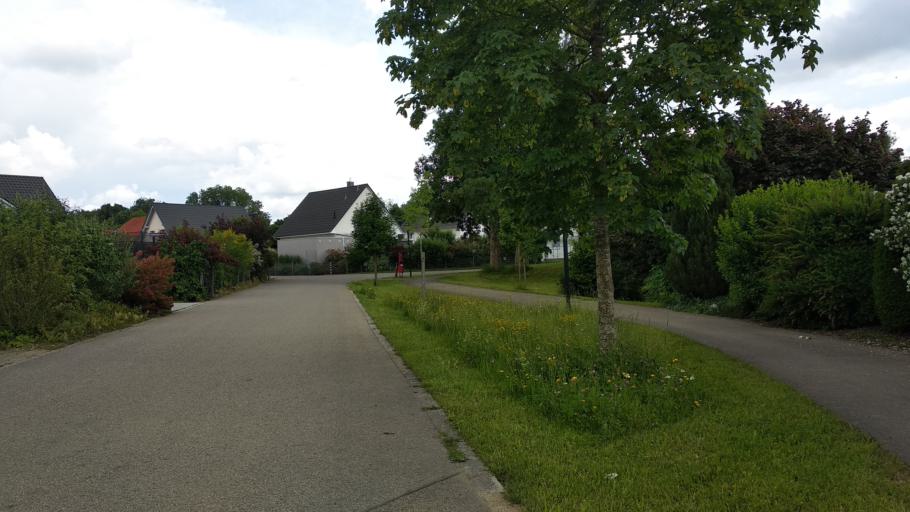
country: DE
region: Baden-Wuerttemberg
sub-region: Tuebingen Region
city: Aitrach
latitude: 47.9385
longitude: 10.0949
